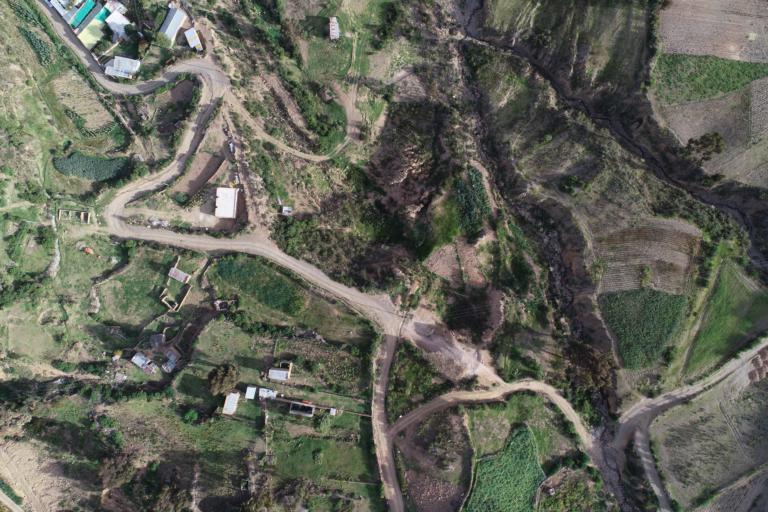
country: BO
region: La Paz
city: La Paz
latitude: -16.5476
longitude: -67.9950
